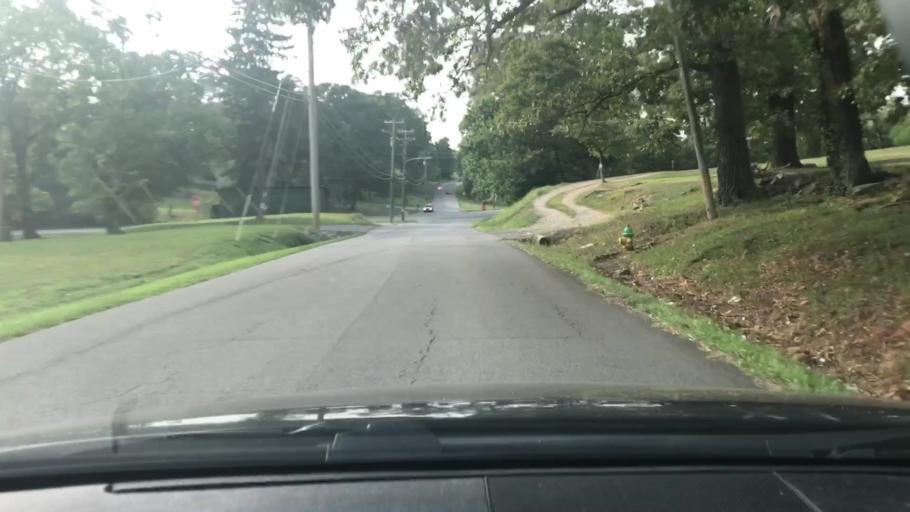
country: US
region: Tennessee
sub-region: Dickson County
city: White Bluff
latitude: 36.1117
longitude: -87.2255
